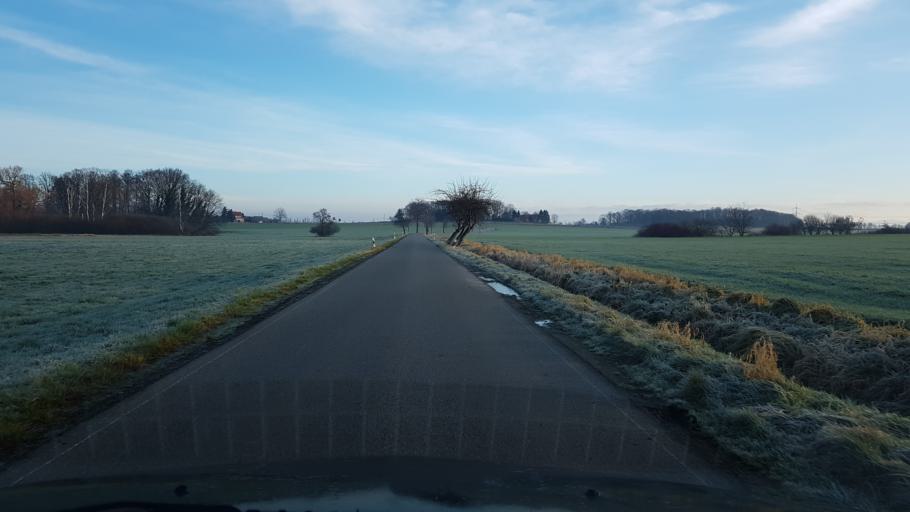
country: DE
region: Saxony
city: Neschwitz
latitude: 51.2453
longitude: 14.3492
